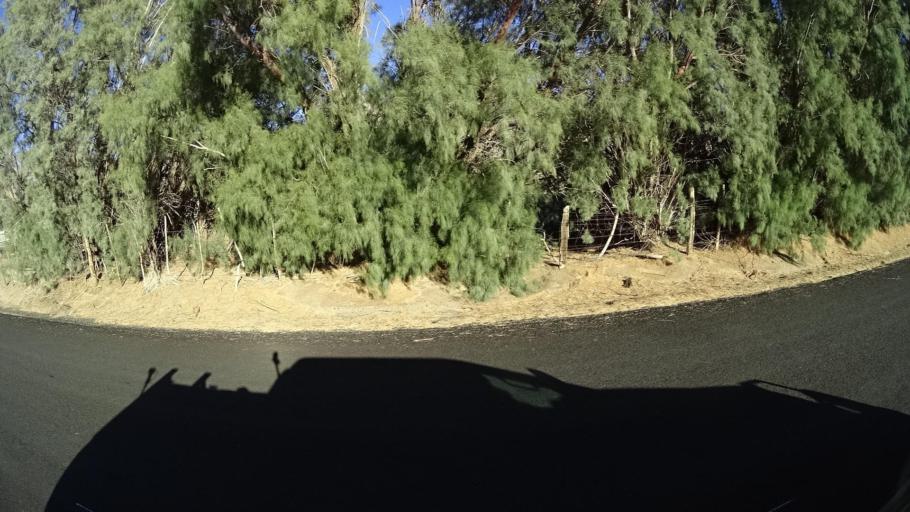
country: US
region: California
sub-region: Kern County
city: Weldon
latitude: 35.6464
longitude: -118.2714
